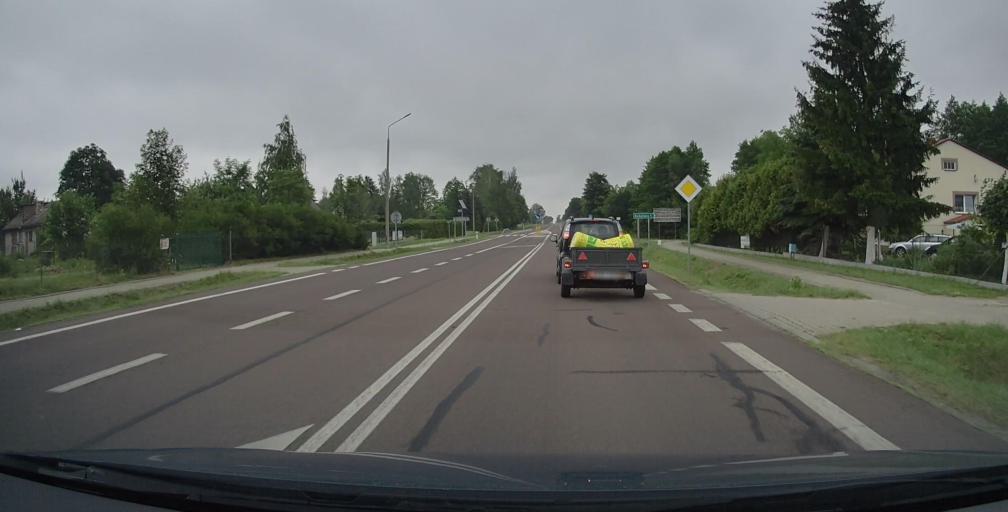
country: PL
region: Lublin Voivodeship
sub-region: Powiat bialski
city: Terespol
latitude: 52.0478
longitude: 23.5475
